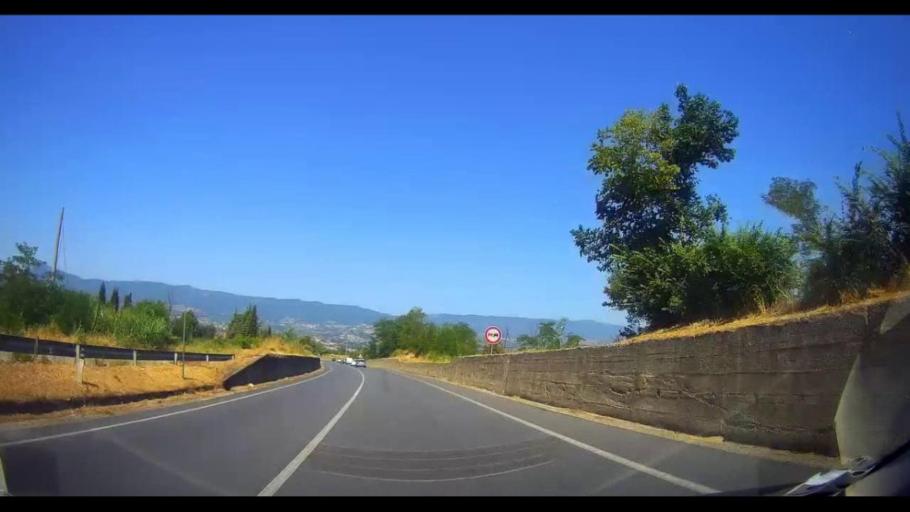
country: IT
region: Calabria
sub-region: Provincia di Cosenza
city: Zumpano
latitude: 39.2991
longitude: 16.2904
